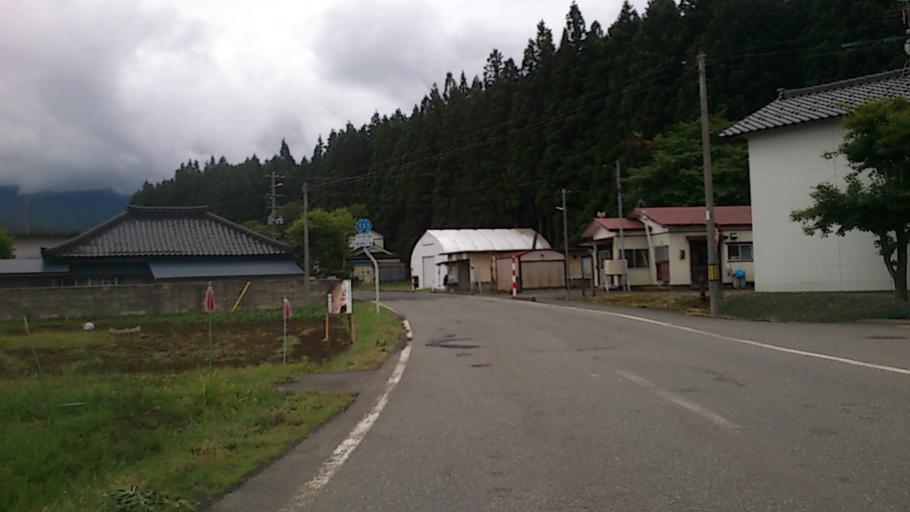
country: JP
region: Yamagata
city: Yuza
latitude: 39.1810
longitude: 139.9461
